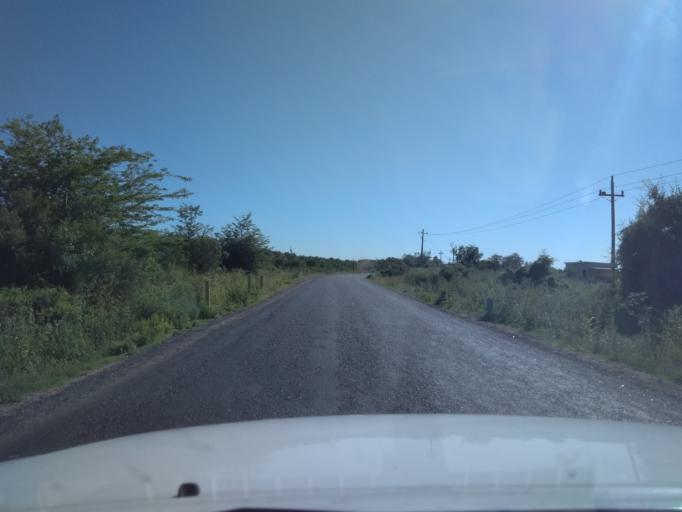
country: UY
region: Canelones
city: San Ramon
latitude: -34.2698
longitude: -55.9405
